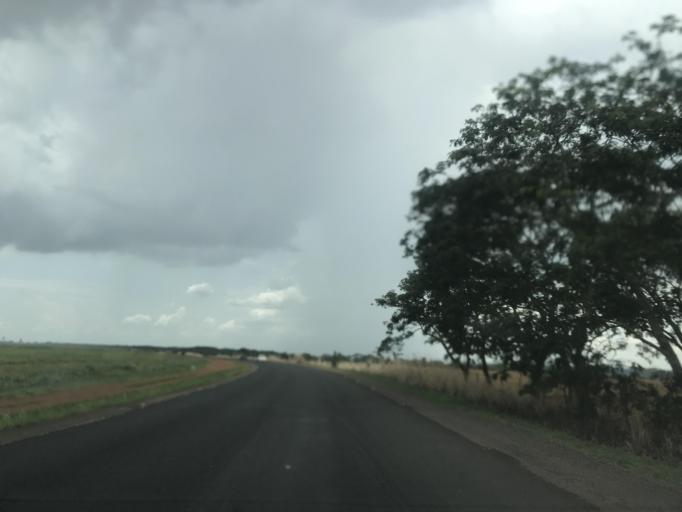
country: BR
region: Goias
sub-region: Vianopolis
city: Vianopolis
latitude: -16.8650
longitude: -48.5496
